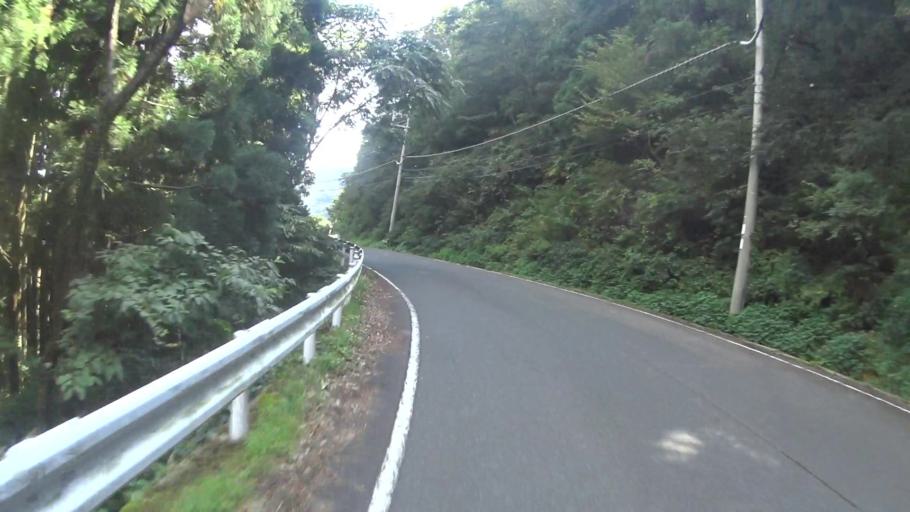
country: JP
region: Kyoto
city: Miyazu
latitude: 35.7129
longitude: 135.1933
